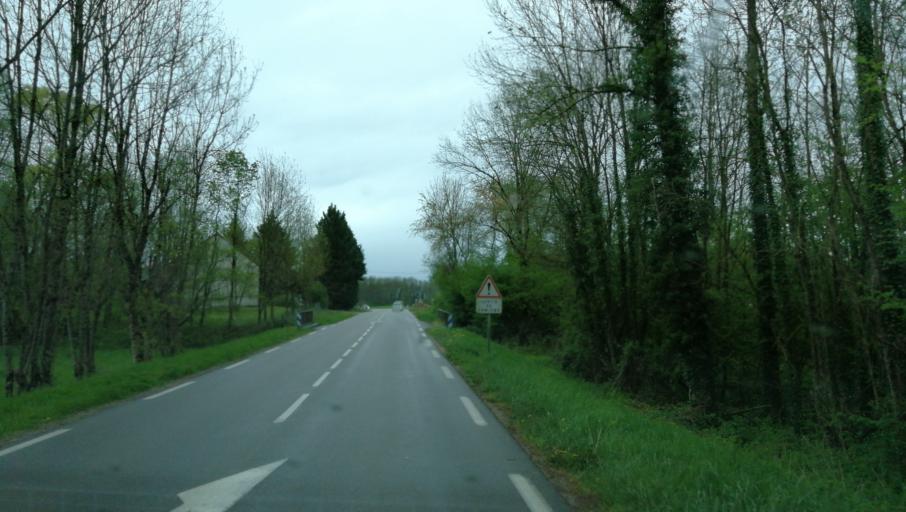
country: FR
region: Franche-Comte
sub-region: Departement du Jura
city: Bletterans
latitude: 46.7189
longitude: 5.4738
